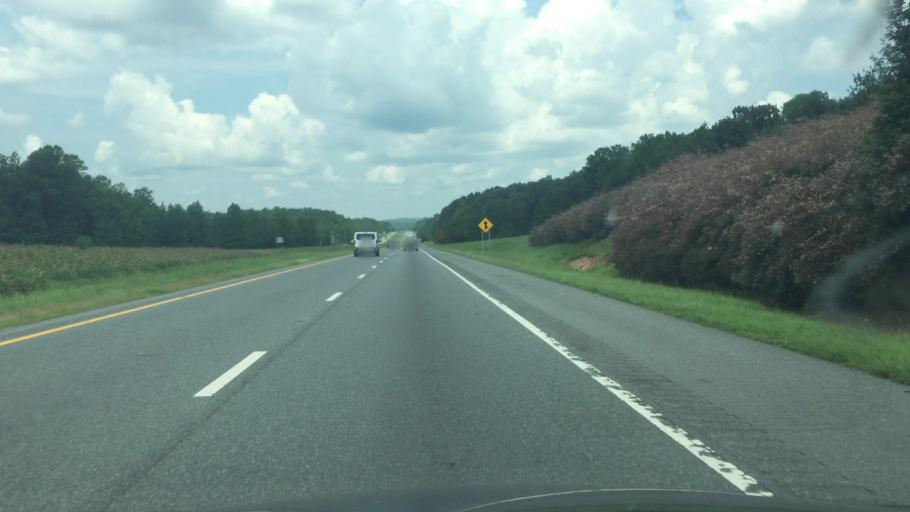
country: US
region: North Carolina
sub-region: Randolph County
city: Asheboro
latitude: 35.5366
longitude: -79.7908
